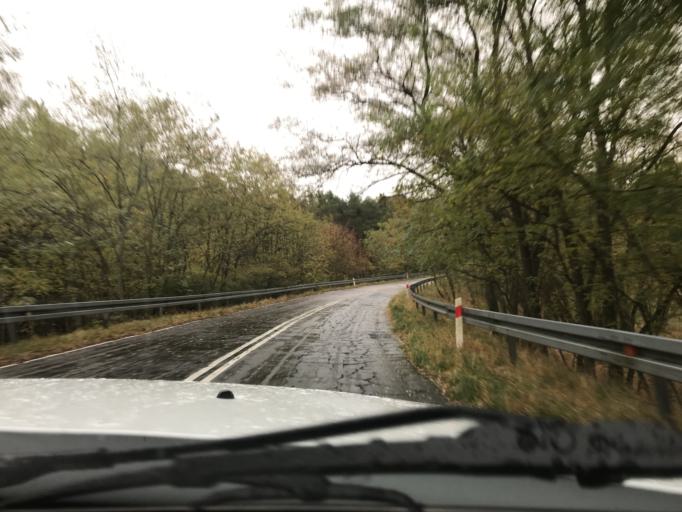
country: DE
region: Brandenburg
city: Neulewin
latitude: 52.7734
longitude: 14.3070
